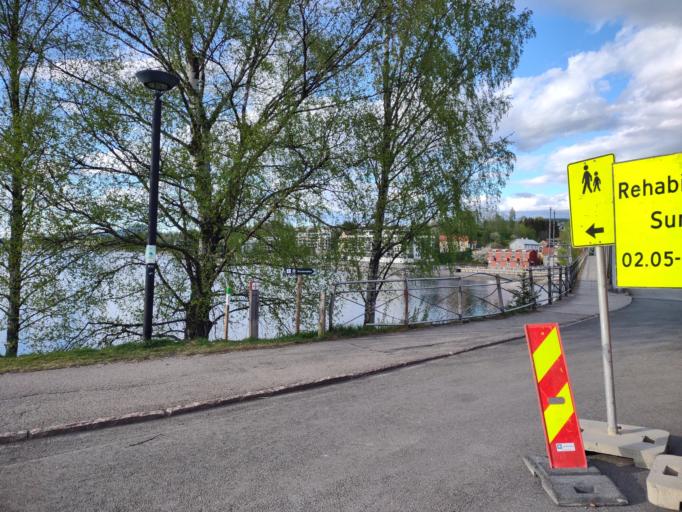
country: NO
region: Akershus
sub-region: Eidsvoll
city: Eidsvoll
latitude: 60.3274
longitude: 11.2533
